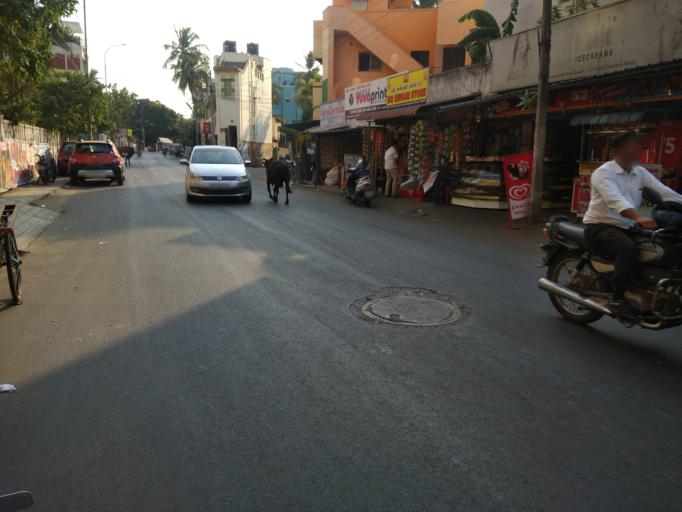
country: IN
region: Tamil Nadu
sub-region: Kancheepuram
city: Madipakkam
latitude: 12.9811
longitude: 80.1852
